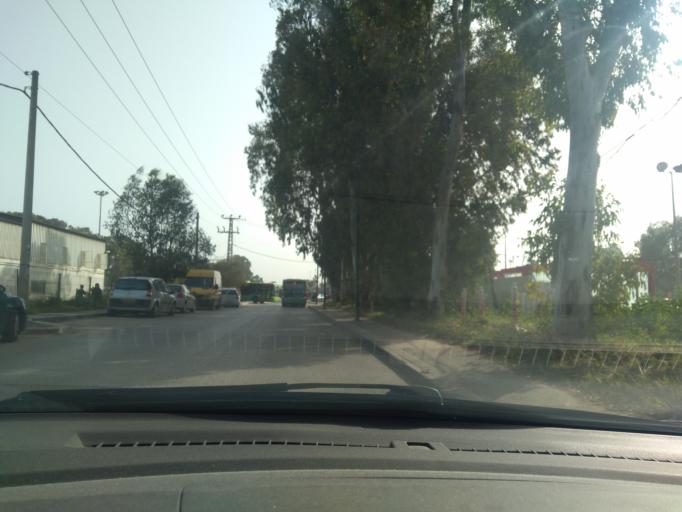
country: IL
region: Central District
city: Netanya
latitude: 32.3214
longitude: 34.8682
